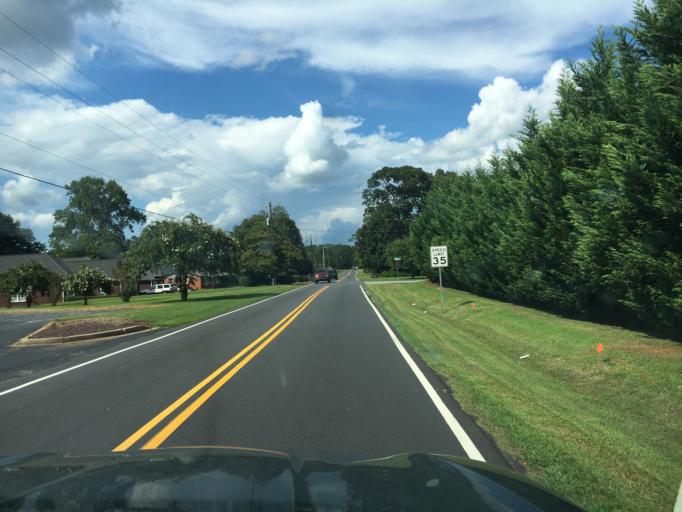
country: US
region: South Carolina
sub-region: Spartanburg County
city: Southern Shops
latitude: 35.0036
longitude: -81.9905
